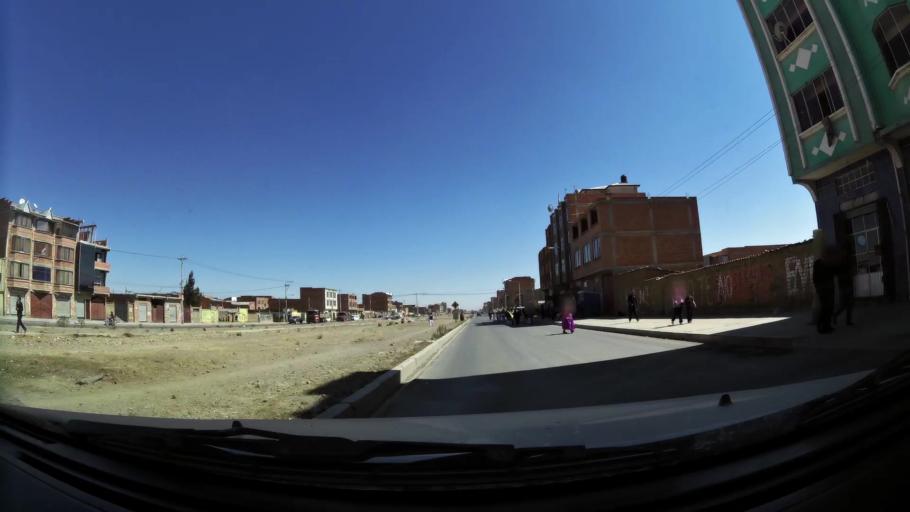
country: BO
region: La Paz
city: La Paz
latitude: -16.5404
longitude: -68.2004
